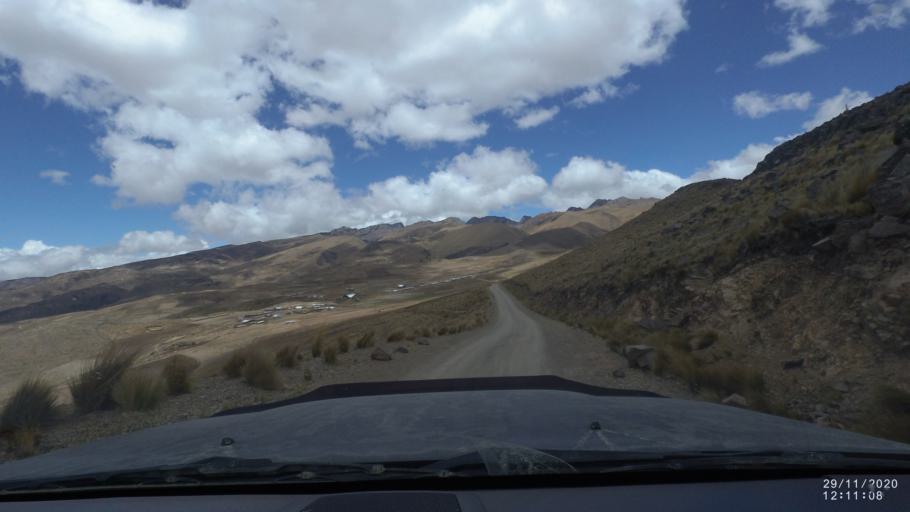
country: BO
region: Cochabamba
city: Cochabamba
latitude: -17.1212
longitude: -66.3062
